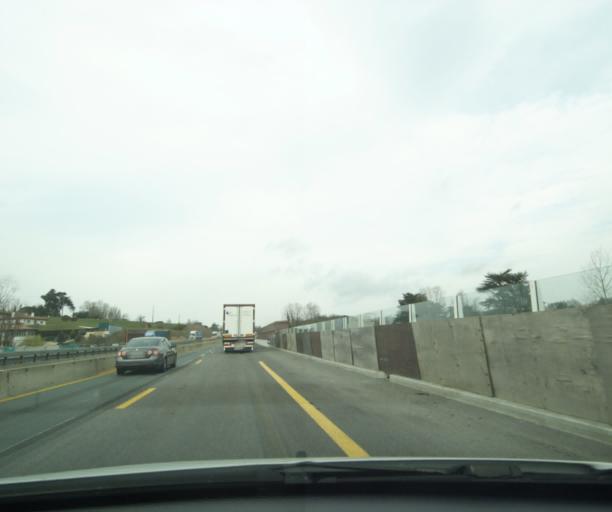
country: FR
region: Aquitaine
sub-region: Departement des Pyrenees-Atlantiques
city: Saint-Jean-de-Luz
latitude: 43.3824
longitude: -1.6440
